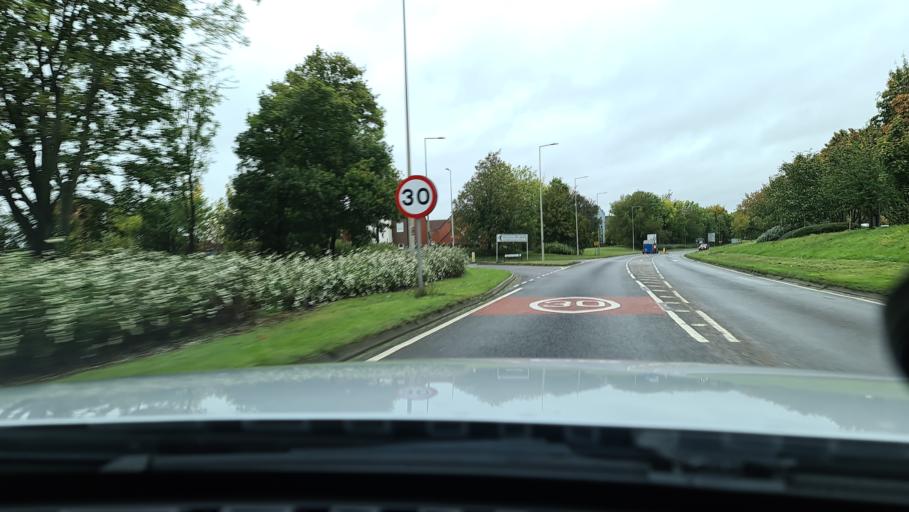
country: GB
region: England
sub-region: Milton Keynes
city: Stony Stratford
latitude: 52.0591
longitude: -0.8282
